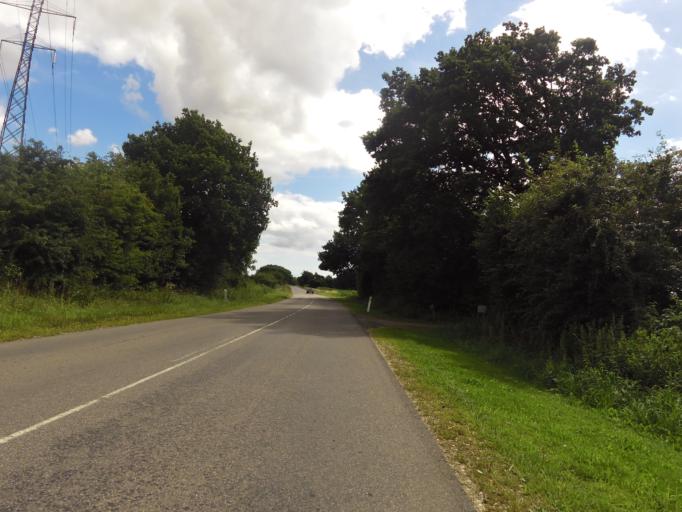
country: DK
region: South Denmark
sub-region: Haderslev Kommune
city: Haderslev
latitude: 55.2794
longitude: 9.4103
